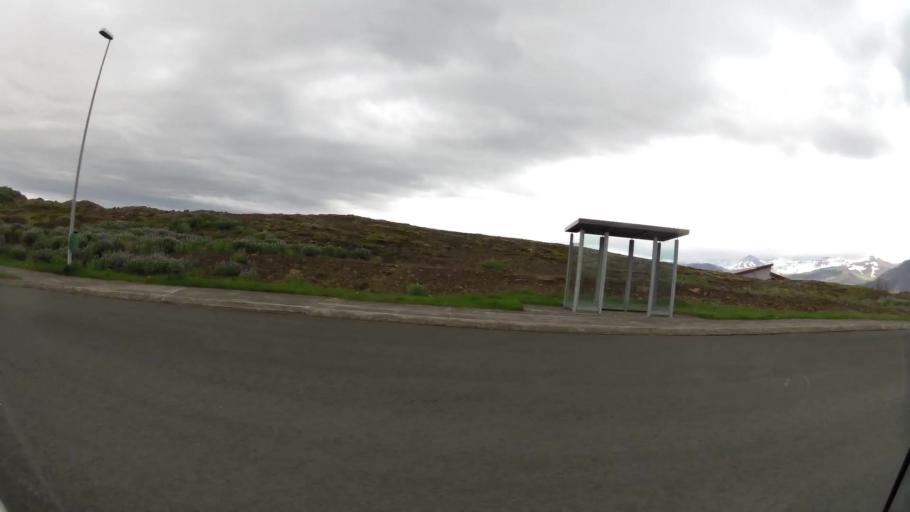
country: IS
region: West
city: Borgarnes
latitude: 64.5558
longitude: -21.8956
